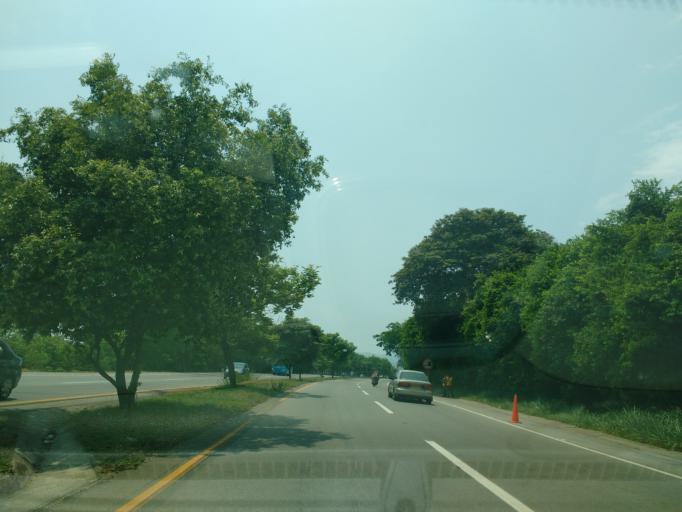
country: CO
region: Tolima
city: Melgar
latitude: 4.2183
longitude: -74.6904
